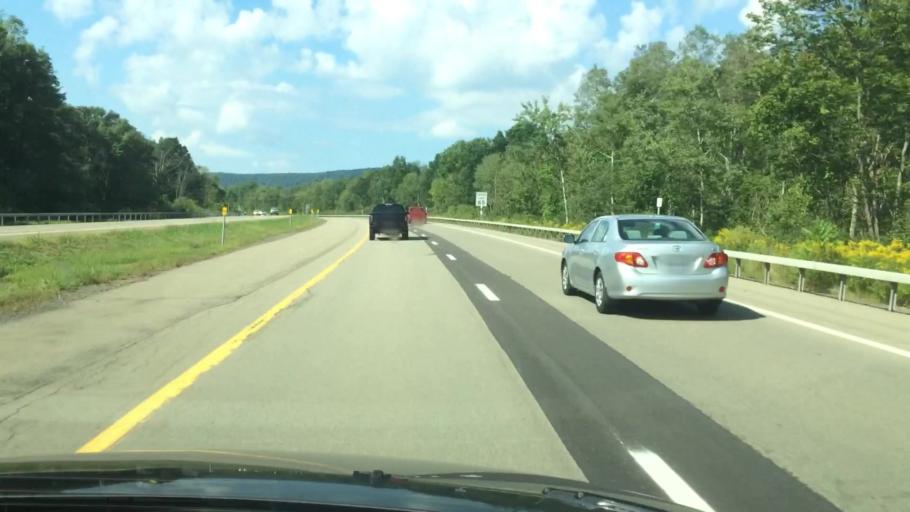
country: US
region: New York
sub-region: Cattaraugus County
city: Salamanca
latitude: 42.1516
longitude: -78.7604
